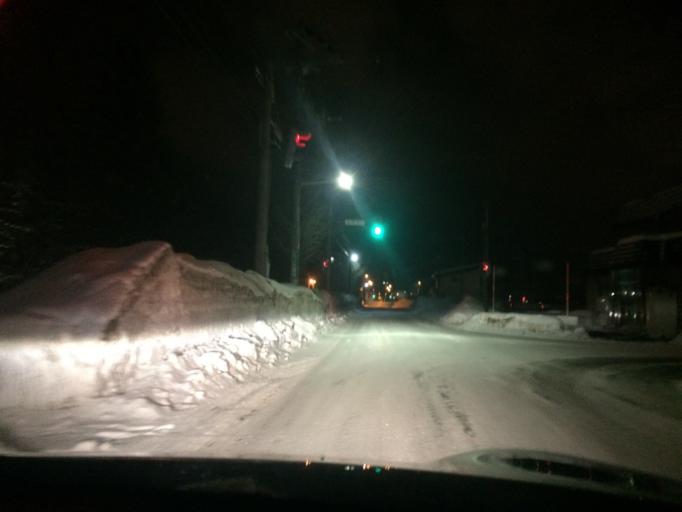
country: JP
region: Hokkaido
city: Sapporo
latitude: 43.0700
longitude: 141.3883
